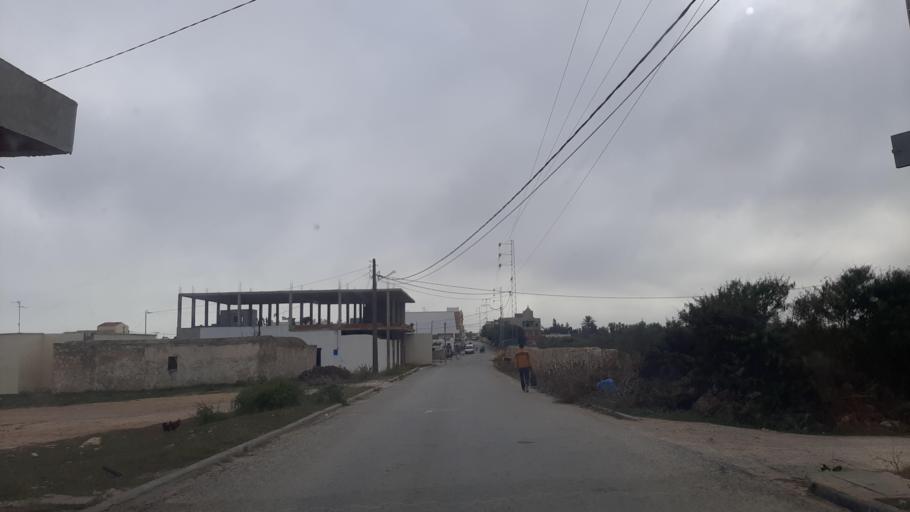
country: TN
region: Nabul
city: Menzel Heurr
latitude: 36.6819
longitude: 10.9266
